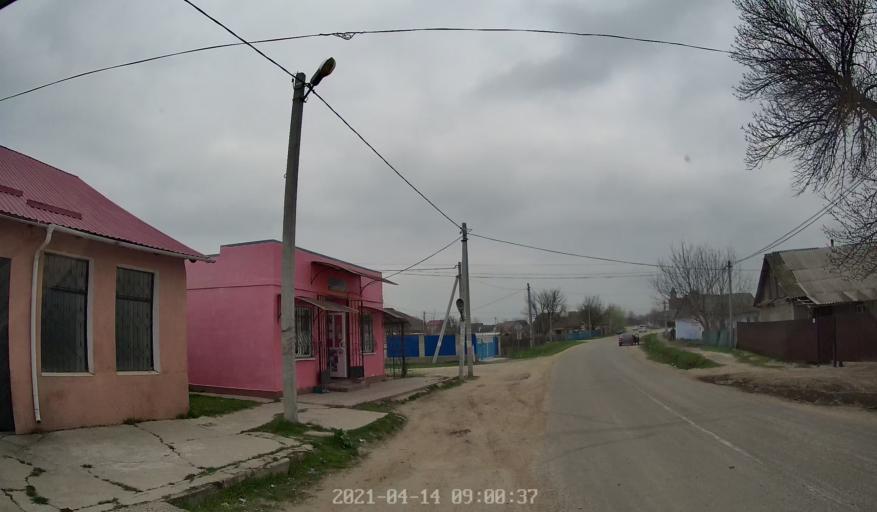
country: MD
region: Chisinau
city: Vadul lui Voda
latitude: 47.0997
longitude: 29.1120
